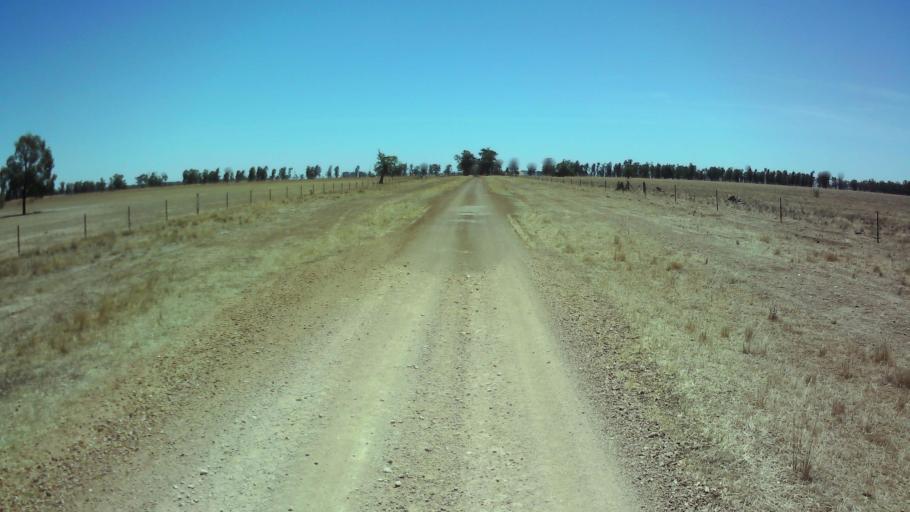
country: AU
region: New South Wales
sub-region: Weddin
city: Grenfell
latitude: -33.9767
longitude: 147.7370
